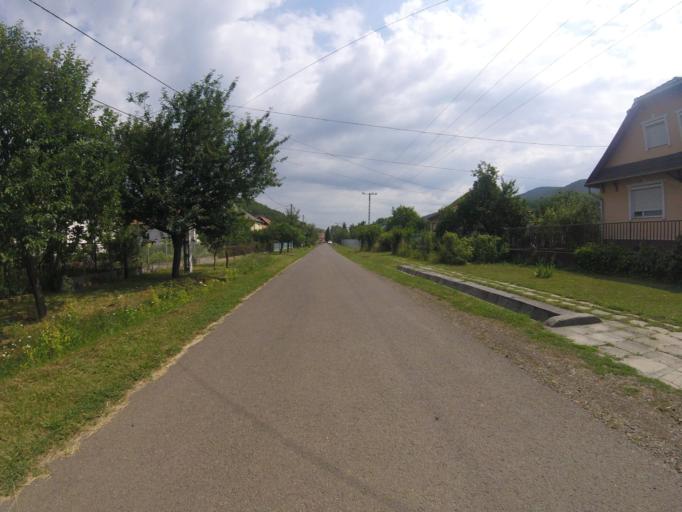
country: HU
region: Nograd
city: Tar
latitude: 47.9583
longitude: 19.7487
